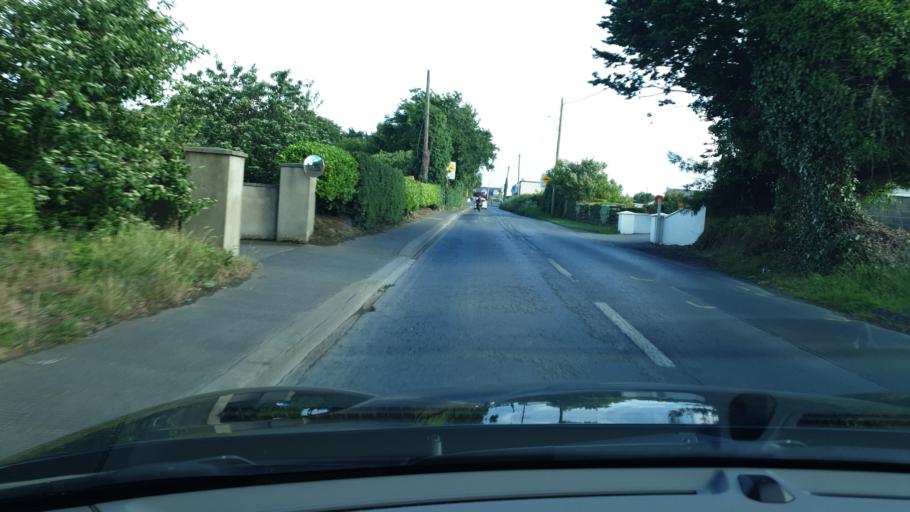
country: IE
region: Leinster
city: An Ros
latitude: 53.5492
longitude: -6.1017
